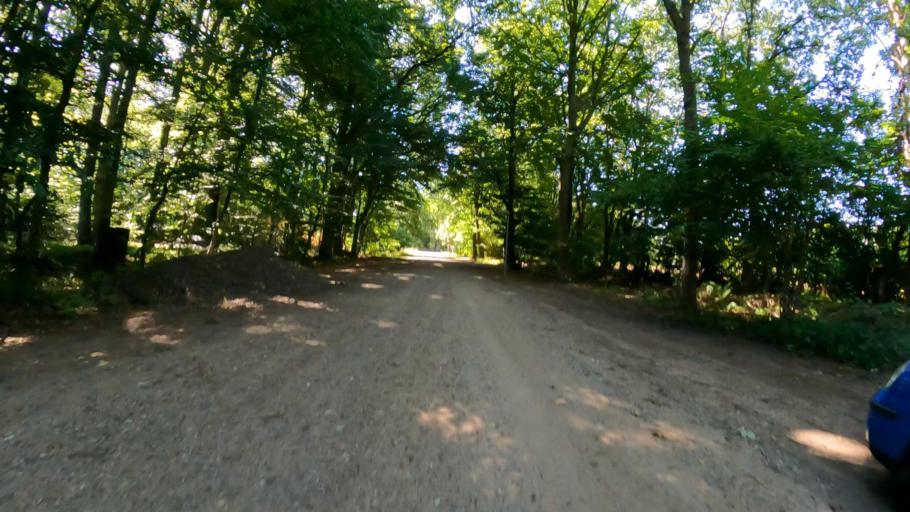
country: DE
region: Schleswig-Holstein
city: Kroppelshagen-Fahrendorf
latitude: 53.4909
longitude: 10.3336
